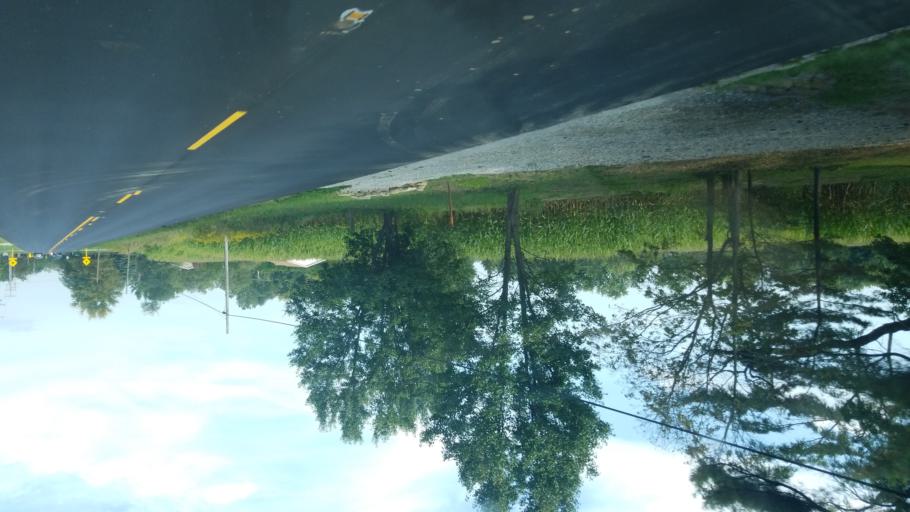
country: US
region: Ohio
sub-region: Franklin County
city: New Albany
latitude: 40.1084
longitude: -82.7752
